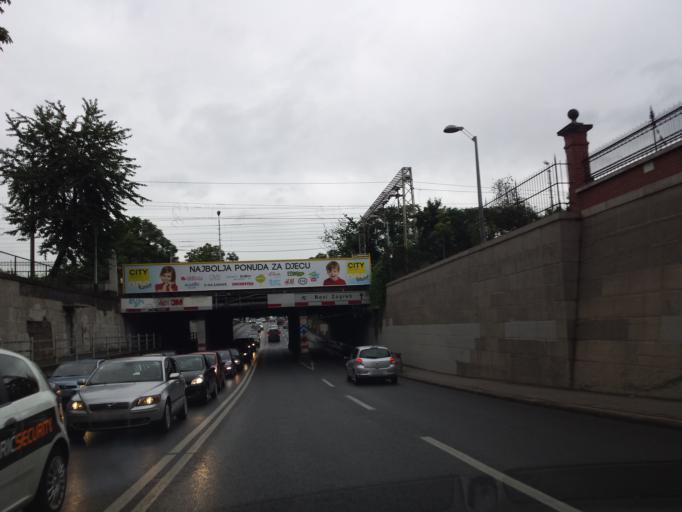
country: HR
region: Grad Zagreb
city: Zagreb - Centar
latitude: 45.8048
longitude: 15.9742
